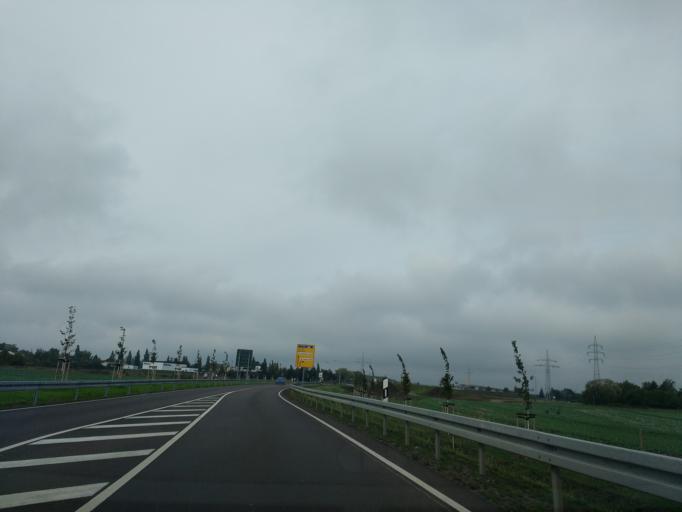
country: DE
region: Saxony-Anhalt
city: Halle (Saale)
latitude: 51.4915
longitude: 12.0169
